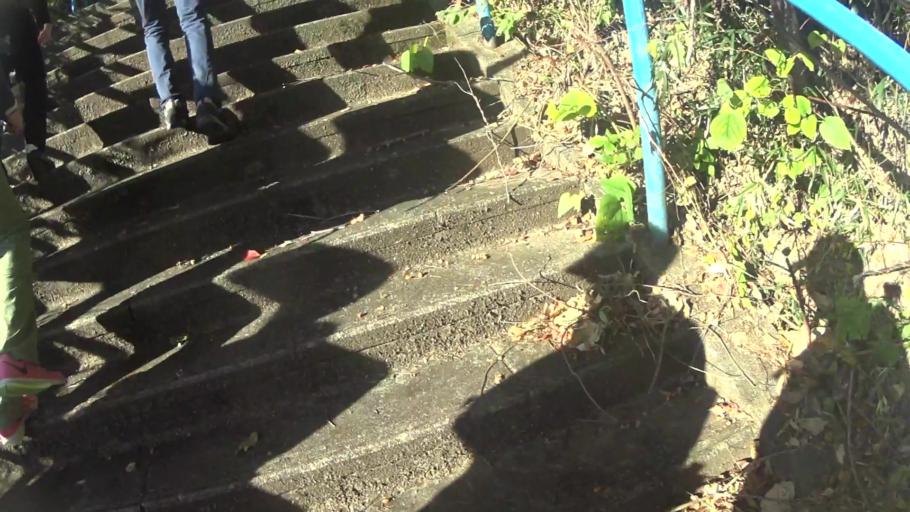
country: JP
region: Tokyo
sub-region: Machida-shi
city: Machida
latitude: 35.6130
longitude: 139.4792
